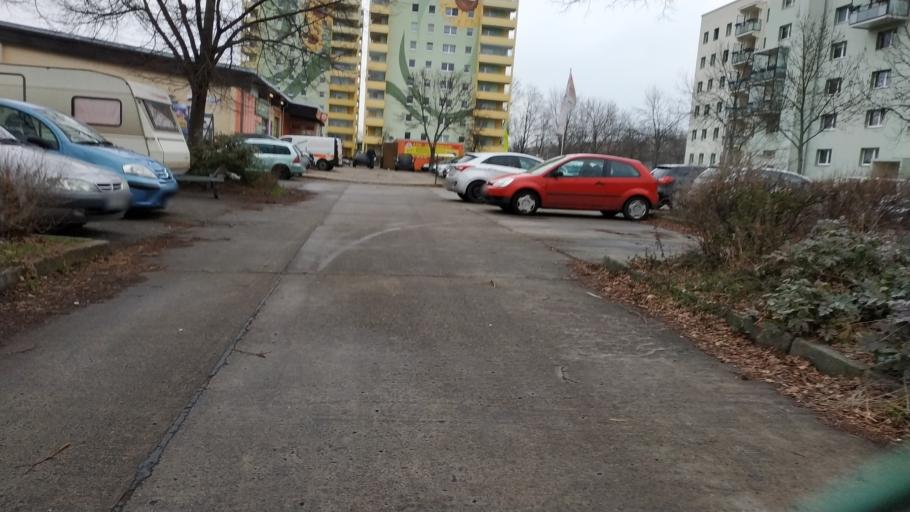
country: DE
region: Berlin
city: Marzahn
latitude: 52.5447
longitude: 13.5847
